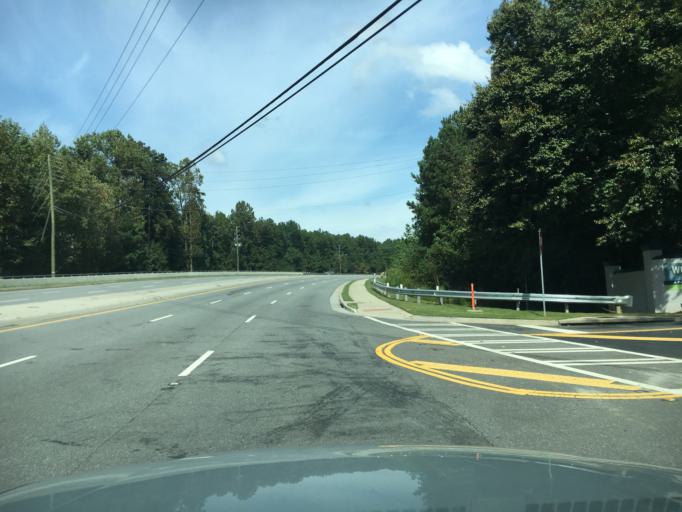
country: US
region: Georgia
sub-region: Gwinnett County
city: Duluth
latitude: 33.9928
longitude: -84.1617
